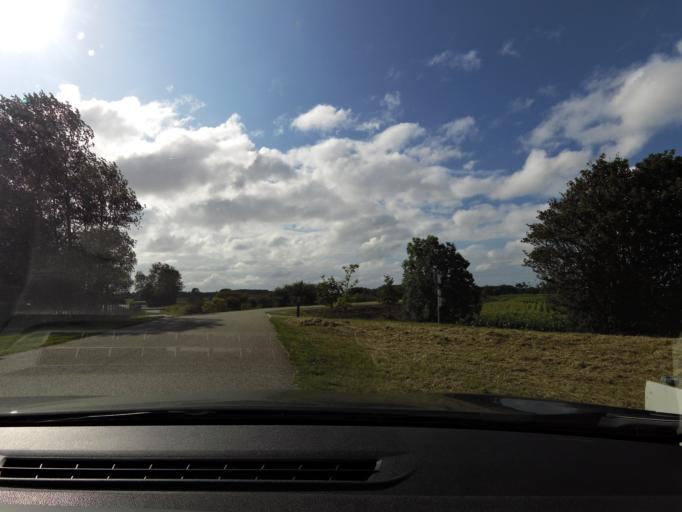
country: NL
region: South Holland
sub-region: Gemeente Goeree-Overflakkee
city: Goedereede
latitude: 51.8149
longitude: 3.9660
